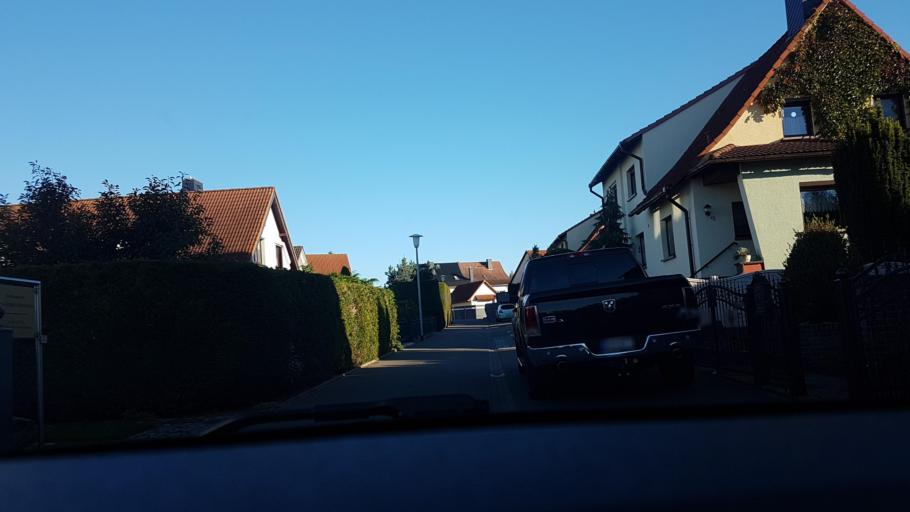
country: DE
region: Saxony-Anhalt
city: Bernburg
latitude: 51.7851
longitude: 11.7295
